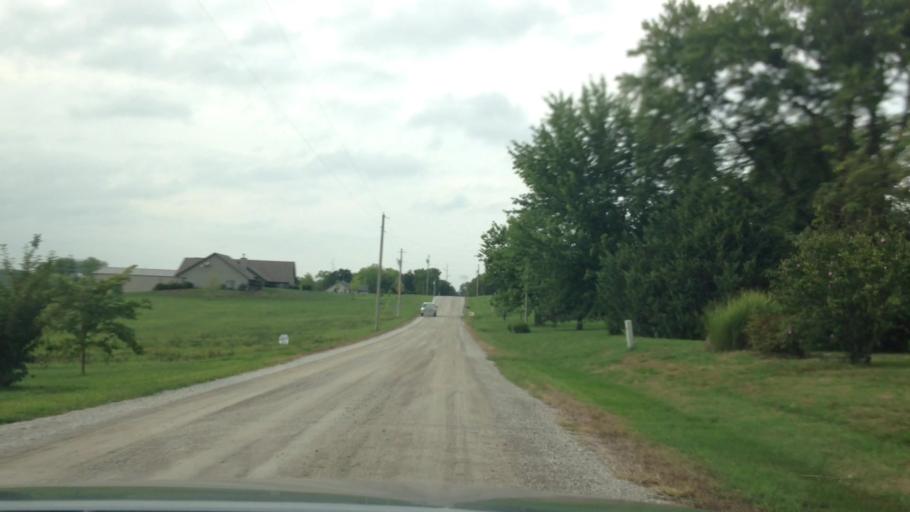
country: US
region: Missouri
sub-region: Clay County
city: Smithville
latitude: 39.4007
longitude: -94.6435
